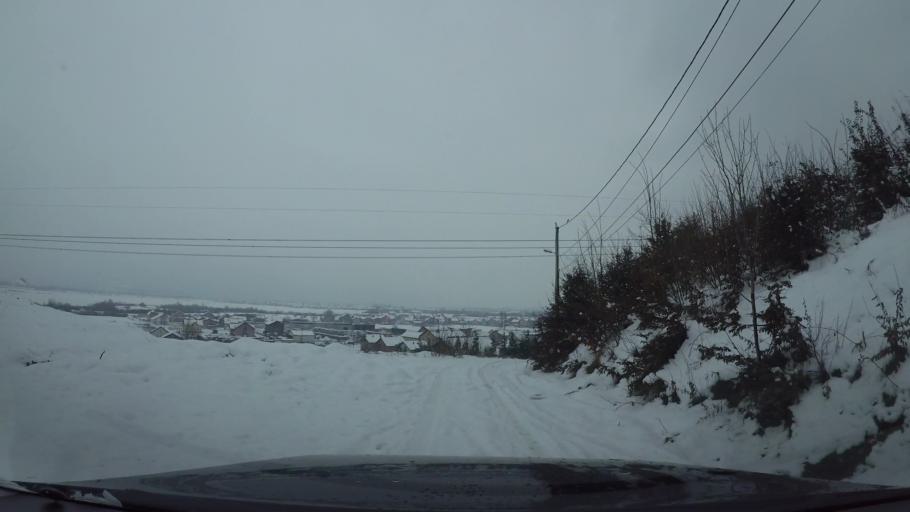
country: BA
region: Federation of Bosnia and Herzegovina
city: Hadzici
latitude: 43.8567
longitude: 18.2695
